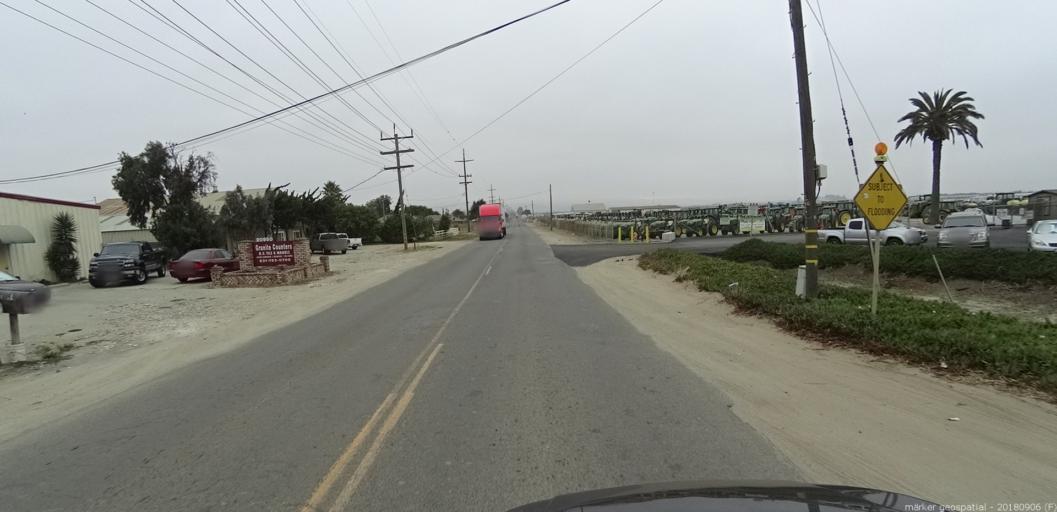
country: US
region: California
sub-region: Monterey County
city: Chualar
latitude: 36.6135
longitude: -121.5660
